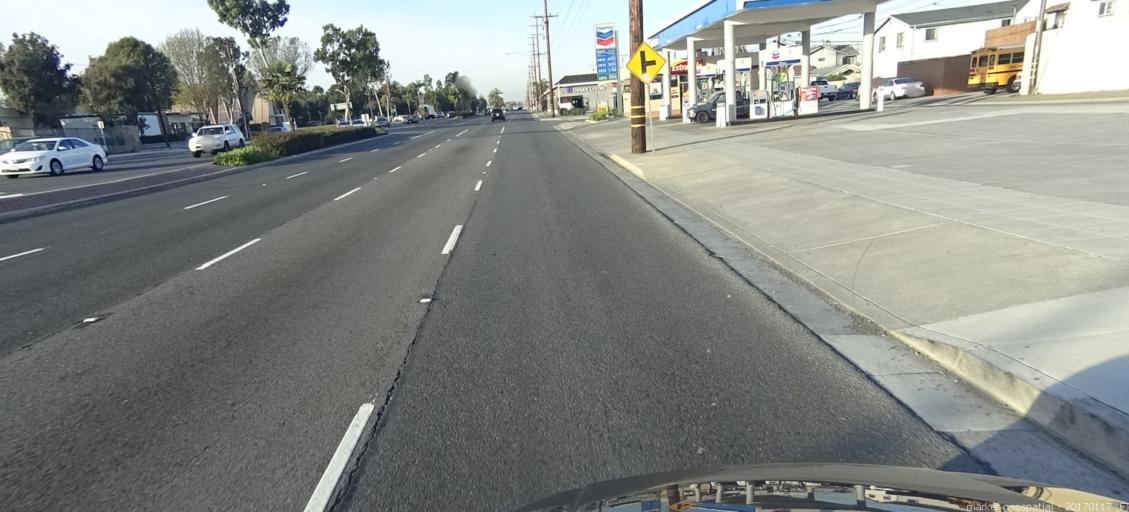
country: US
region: California
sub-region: Orange County
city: Midway City
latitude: 33.7457
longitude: -117.9894
